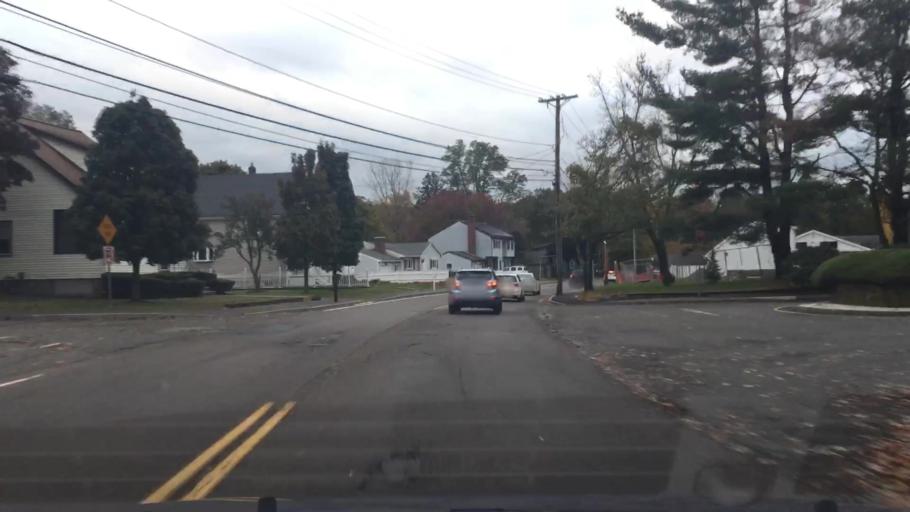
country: US
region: Massachusetts
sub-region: Essex County
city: Saugus
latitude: 42.5004
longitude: -71.0215
